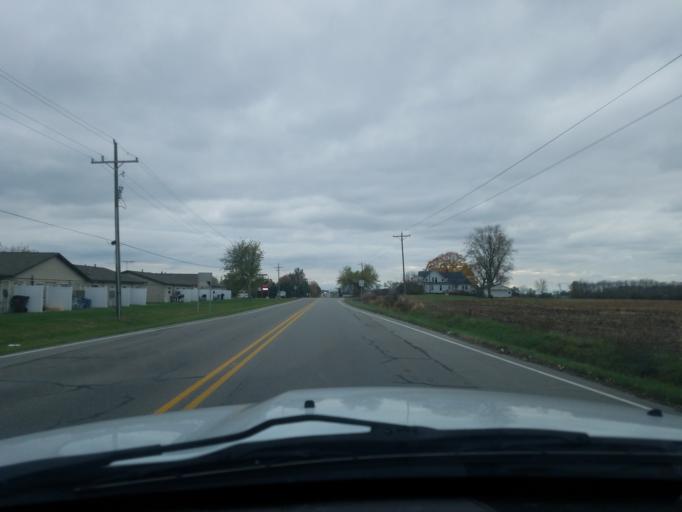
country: US
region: Indiana
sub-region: Bartholomew County
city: Hope
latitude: 39.2891
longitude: -85.7715
